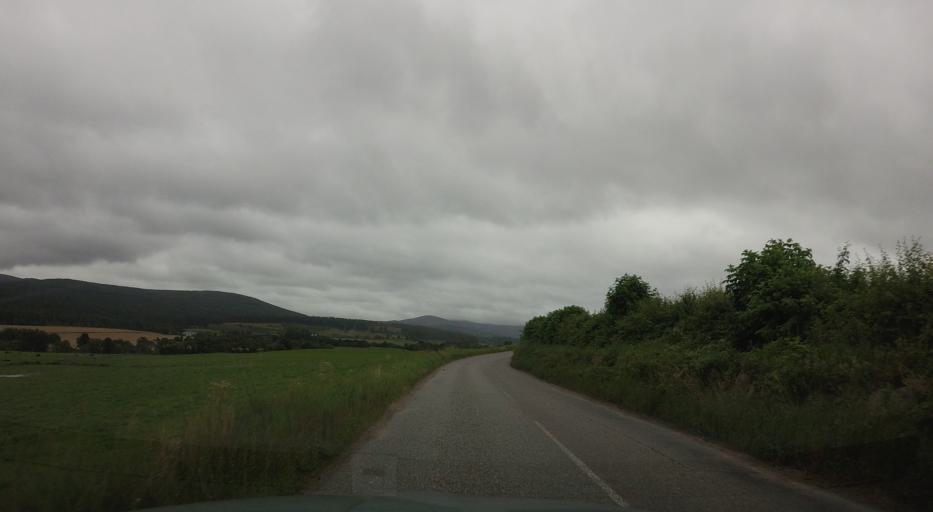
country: GB
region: Scotland
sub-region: Aberdeenshire
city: Banchory
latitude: 57.0261
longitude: -2.5202
